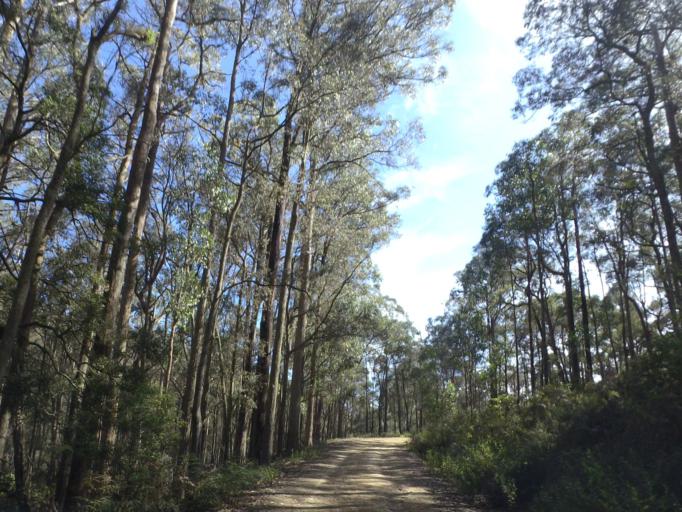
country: AU
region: Victoria
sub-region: Moorabool
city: Bacchus Marsh
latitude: -37.4462
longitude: 144.2623
